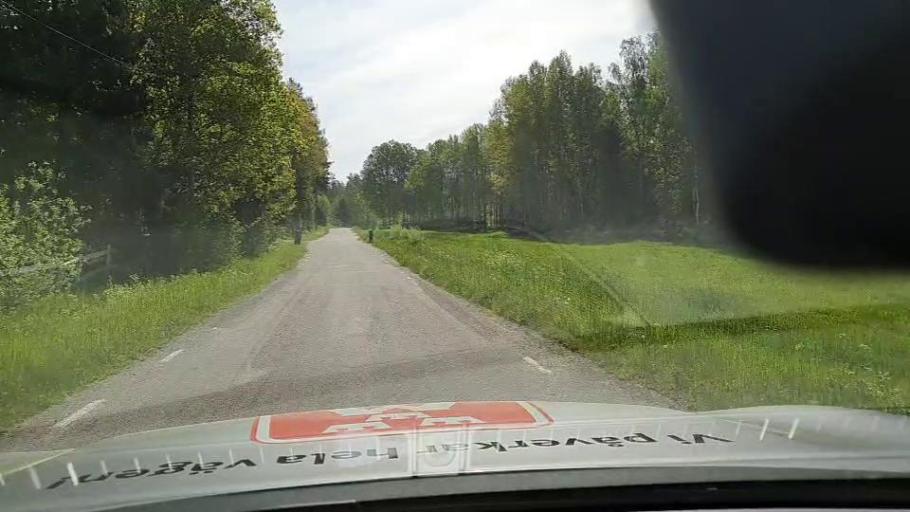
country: SE
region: Soedermanland
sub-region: Eskilstuna Kommun
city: Arla
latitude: 59.2574
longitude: 16.7047
